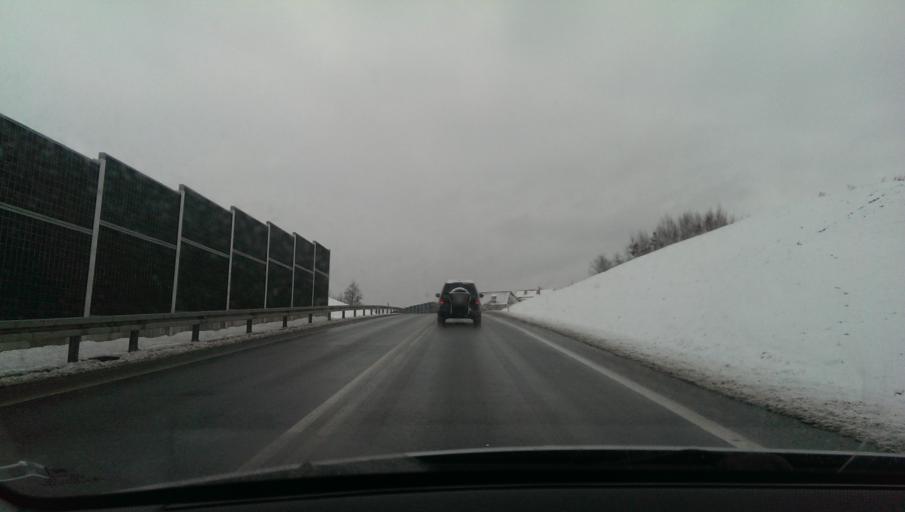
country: PL
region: Subcarpathian Voivodeship
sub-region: Powiat brzozowski
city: Brzozow
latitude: 49.6957
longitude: 22.0335
